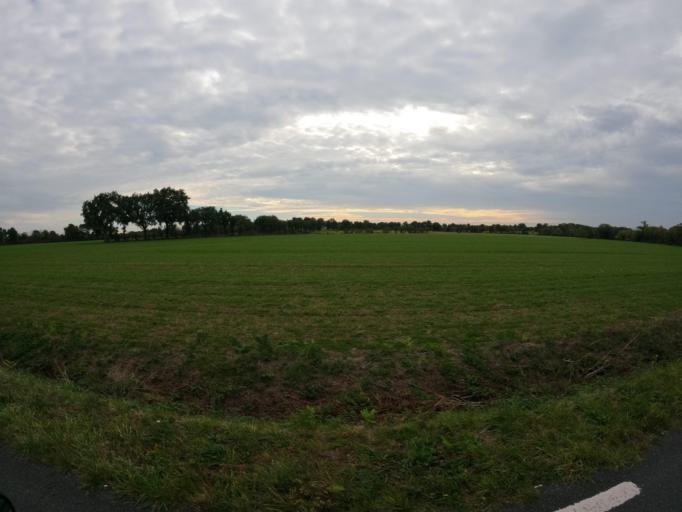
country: FR
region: Pays de la Loire
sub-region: Departement de la Loire-Atlantique
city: Boussay
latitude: 47.0520
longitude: -1.1613
